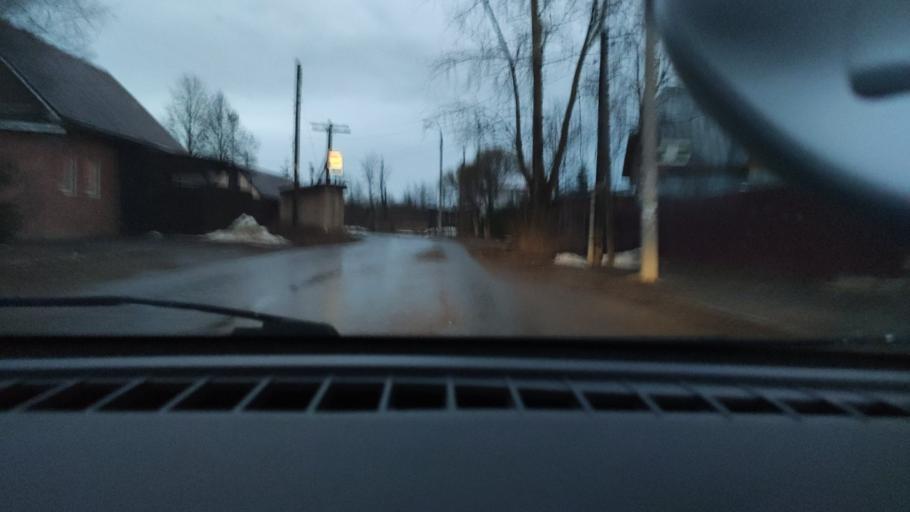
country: RU
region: Perm
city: Perm
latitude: 58.0437
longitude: 56.3514
